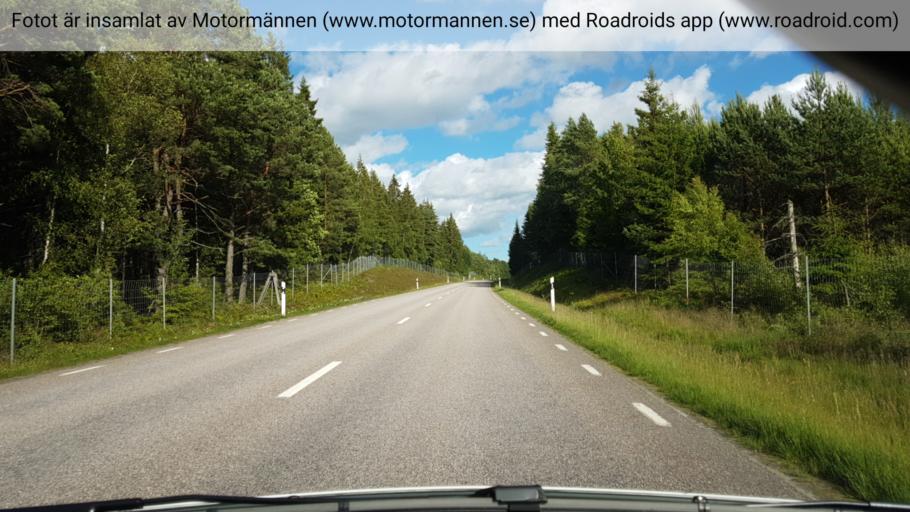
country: SE
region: Vaestra Goetaland
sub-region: Falkopings Kommun
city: Floby
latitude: 58.2056
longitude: 13.2986
